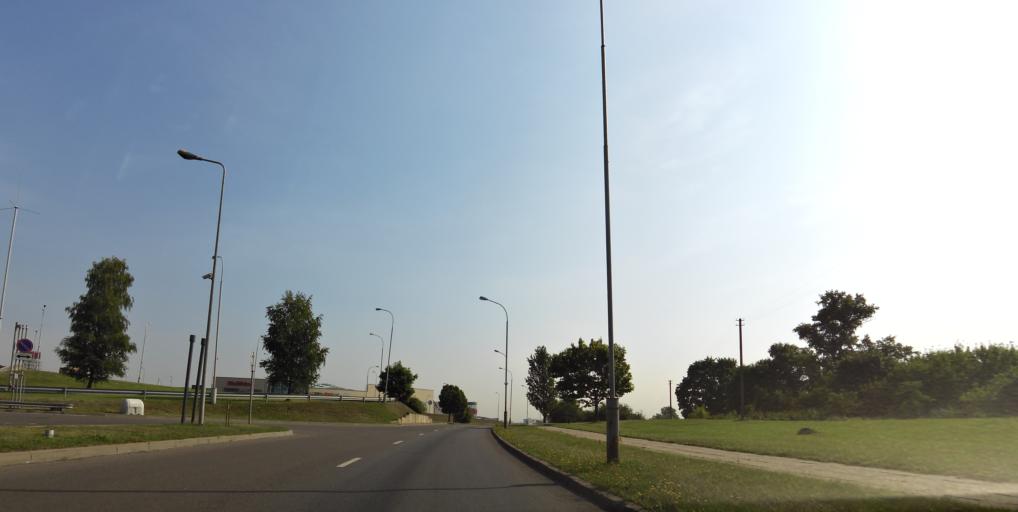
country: LT
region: Vilnius County
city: Seskine
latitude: 54.7117
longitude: 25.2707
